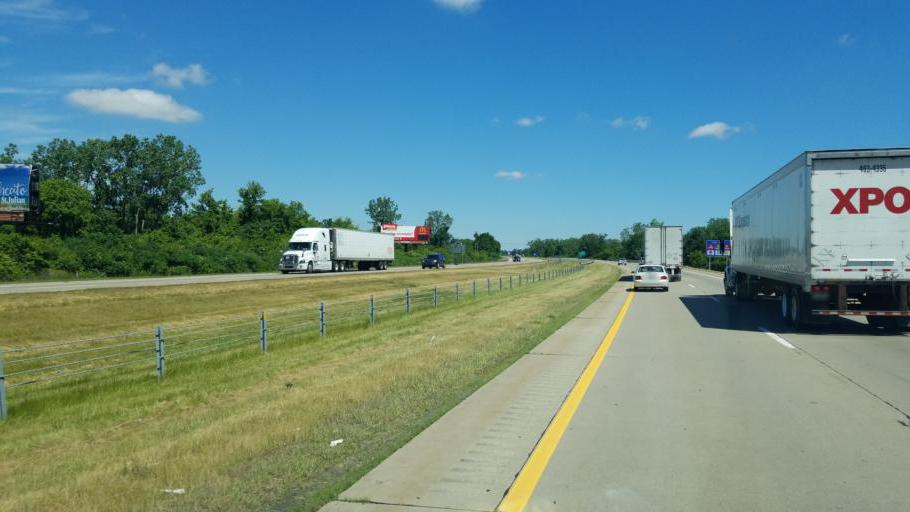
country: US
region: Ohio
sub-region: Lucas County
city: Sylvania
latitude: 41.7302
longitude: -83.6890
